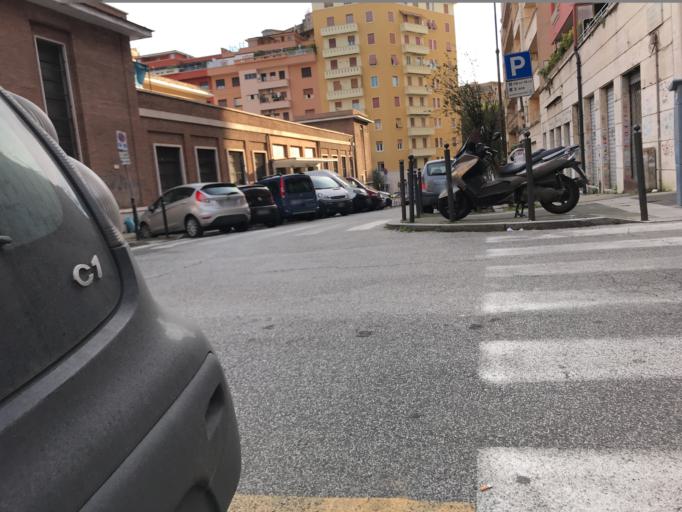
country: IT
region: Latium
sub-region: Citta metropolitana di Roma Capitale
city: Rome
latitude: 41.9091
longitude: 12.5186
